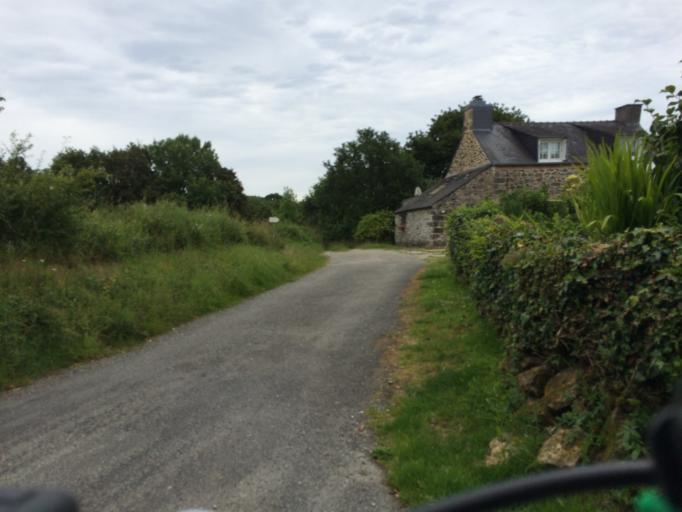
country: FR
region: Brittany
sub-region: Departement du Finistere
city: Hopital-Camfrout
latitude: 48.3256
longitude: -4.2629
